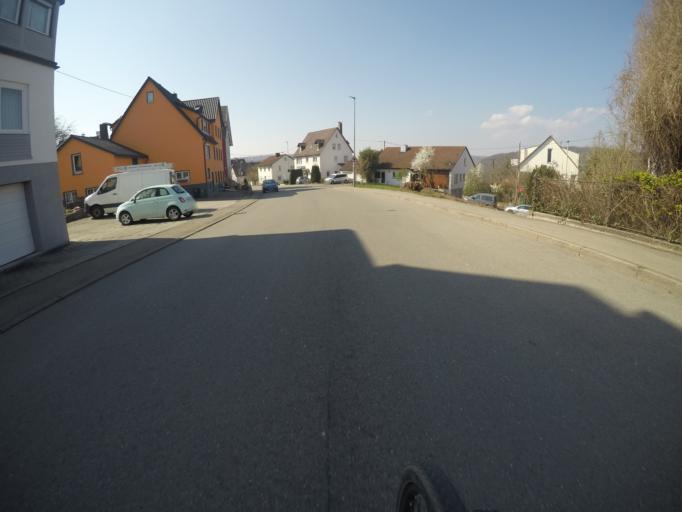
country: DE
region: Baden-Wuerttemberg
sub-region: Tuebingen Region
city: Kirchentellinsfurt
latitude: 48.5339
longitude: 9.1463
